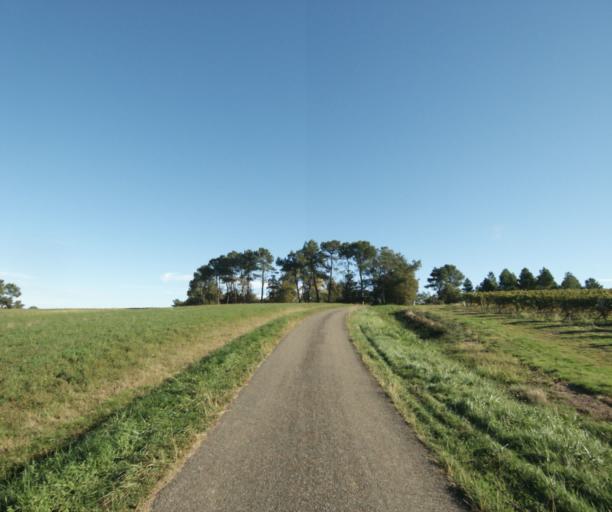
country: FR
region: Midi-Pyrenees
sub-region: Departement du Gers
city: Cazaubon
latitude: 43.8472
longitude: -0.0784
